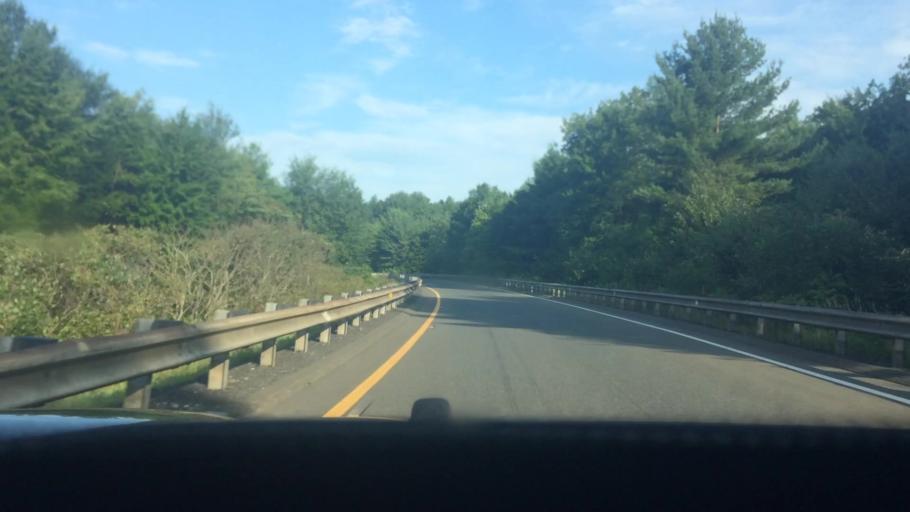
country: US
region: Massachusetts
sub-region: Franklin County
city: Greenfield
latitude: 42.6153
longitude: -72.5920
